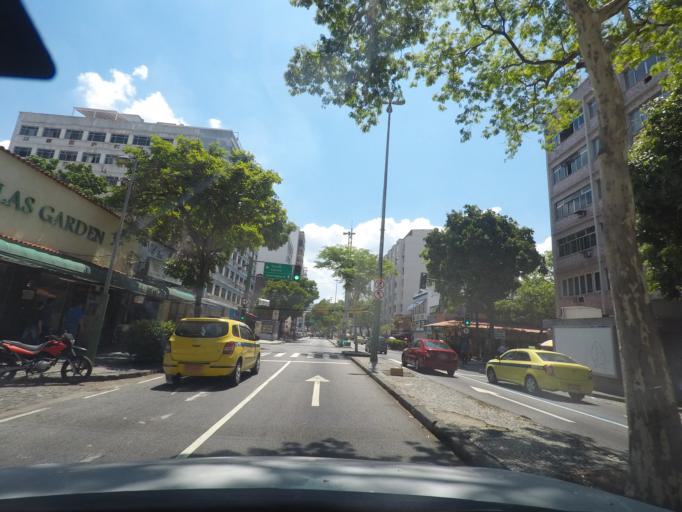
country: BR
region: Rio de Janeiro
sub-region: Rio De Janeiro
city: Rio de Janeiro
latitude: -22.9154
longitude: -43.2436
